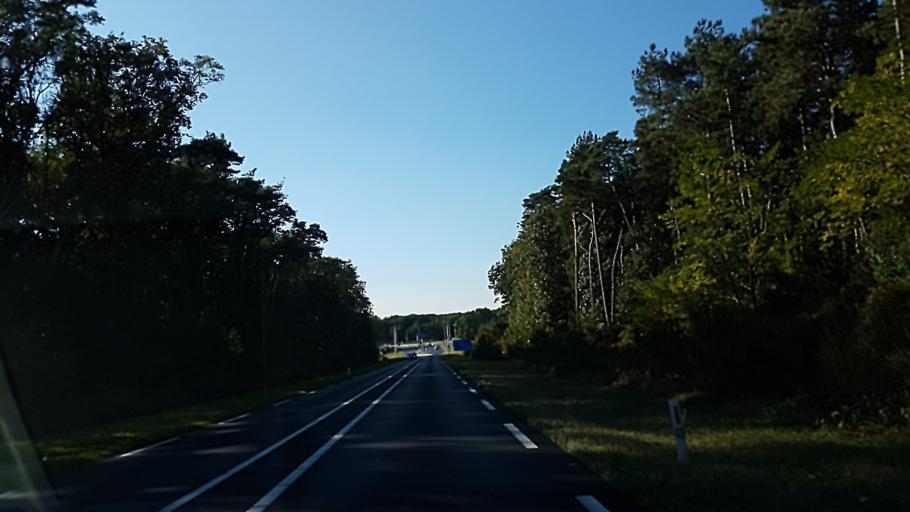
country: NL
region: North Brabant
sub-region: Gemeente Woensdrecht
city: Woensdrecht
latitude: 51.4366
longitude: 4.3238
